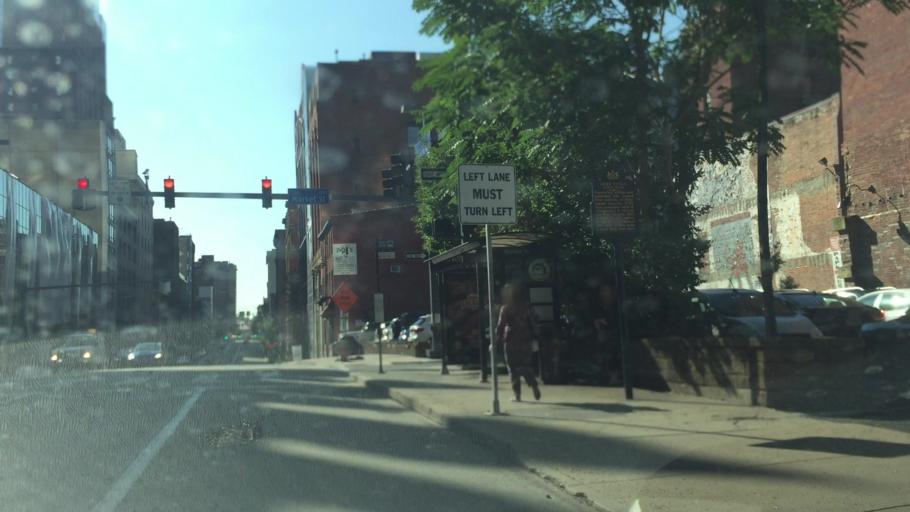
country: US
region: Pennsylvania
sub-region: Allegheny County
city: Pittsburgh
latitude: 40.4392
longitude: -80.0040
